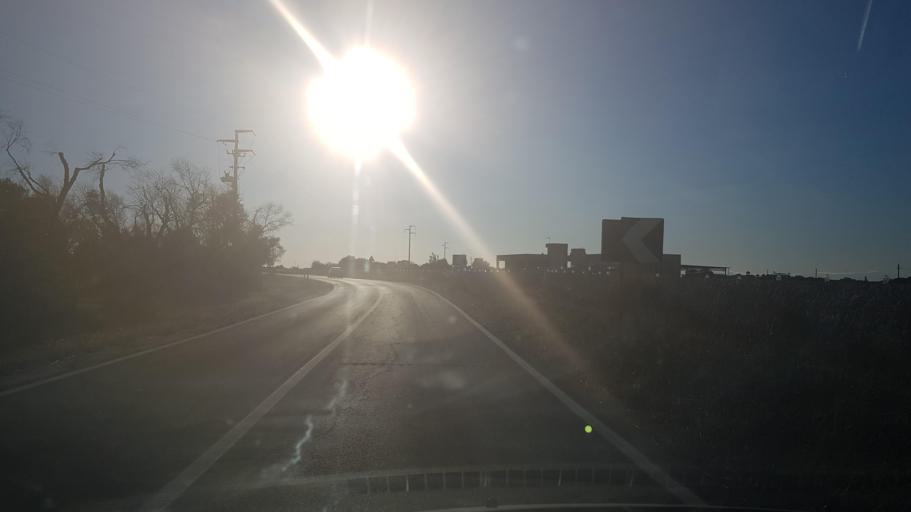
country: IT
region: Apulia
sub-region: Provincia di Lecce
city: Struda
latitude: 40.3290
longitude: 18.3062
